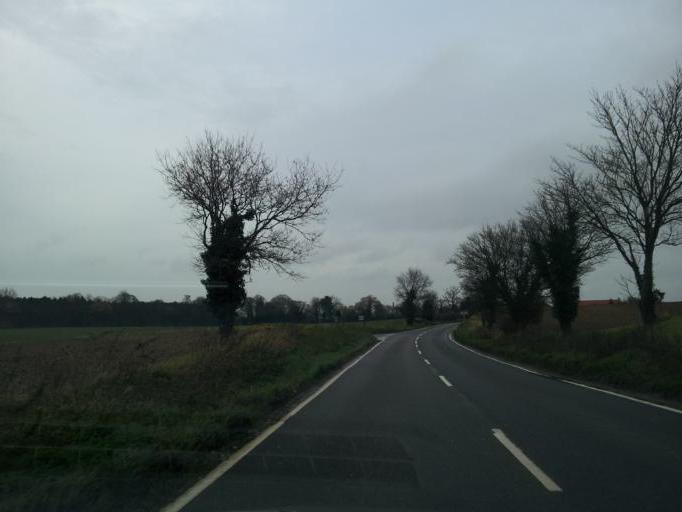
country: GB
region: England
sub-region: Norfolk
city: Acle
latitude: 52.6703
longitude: 1.5907
